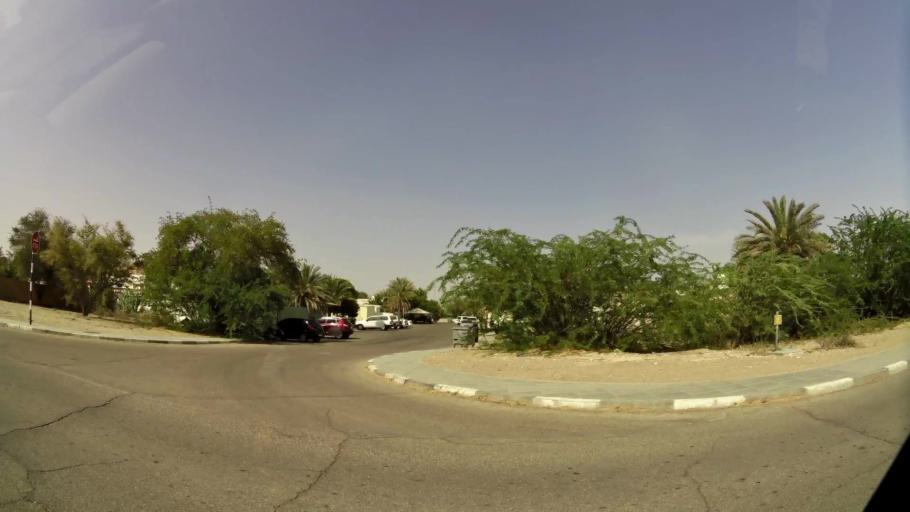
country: AE
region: Abu Dhabi
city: Al Ain
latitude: 24.2353
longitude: 55.7032
